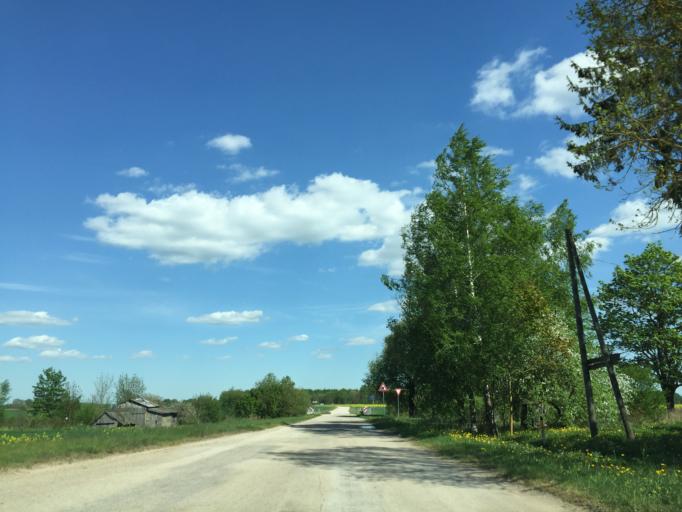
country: LV
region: Rundales
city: Pilsrundale
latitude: 56.3556
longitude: 23.9931
